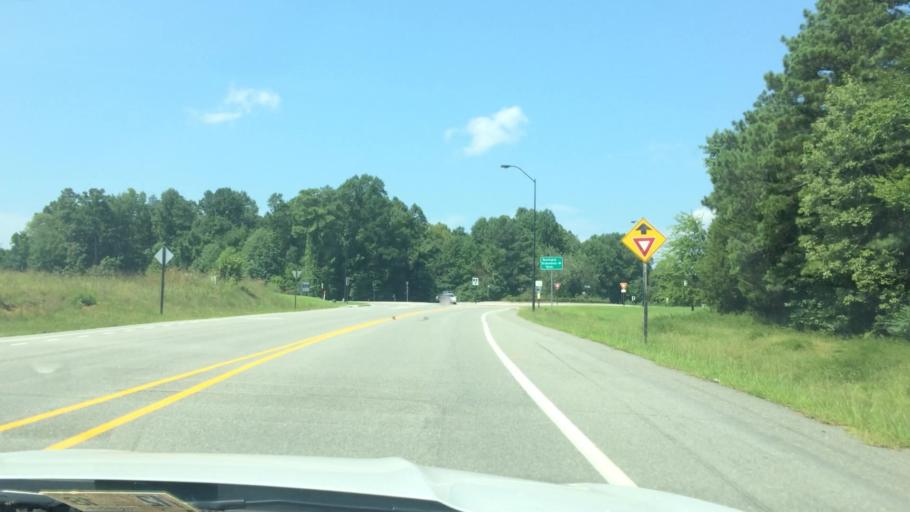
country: US
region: Virginia
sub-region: New Kent County
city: New Kent
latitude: 37.5247
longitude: -77.0741
